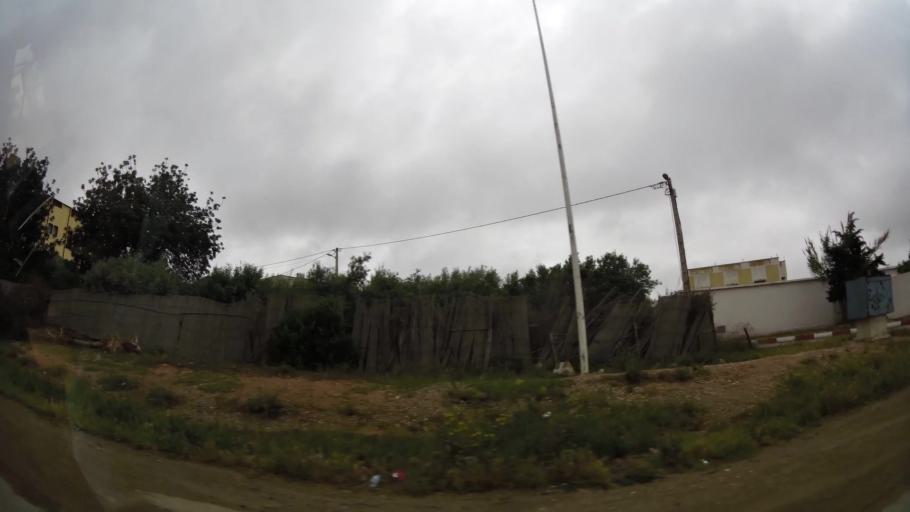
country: MA
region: Oriental
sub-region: Nador
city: Midar
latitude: 35.0546
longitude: -3.4626
